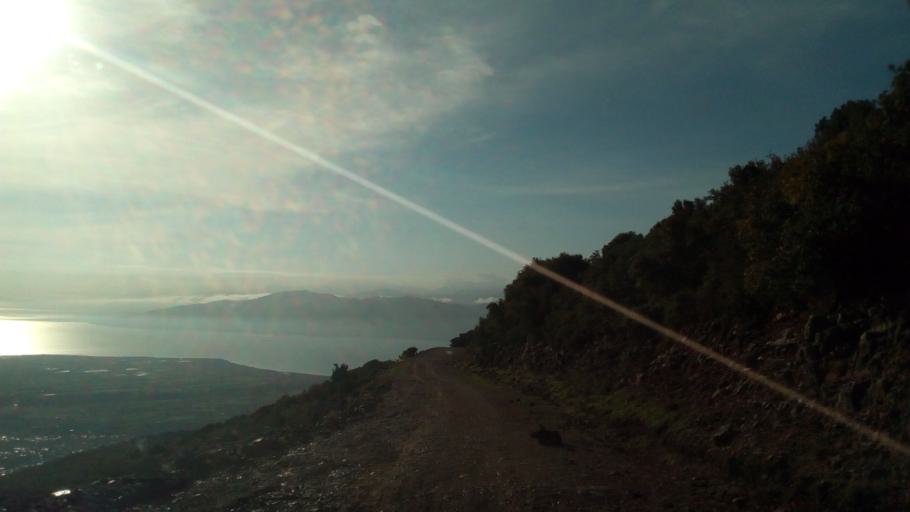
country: GR
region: West Greece
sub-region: Nomos Aitolias kai Akarnanias
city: Nafpaktos
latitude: 38.4119
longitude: 21.8229
